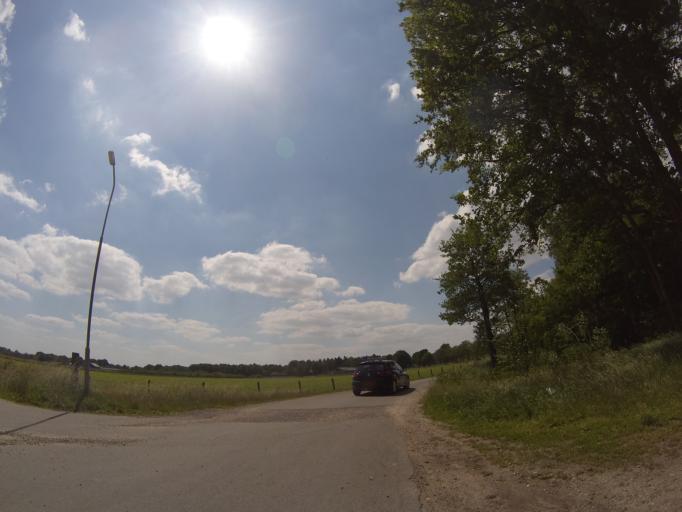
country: NL
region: Gelderland
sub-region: Gemeente Barneveld
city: Stroe
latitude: 52.1859
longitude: 5.6844
